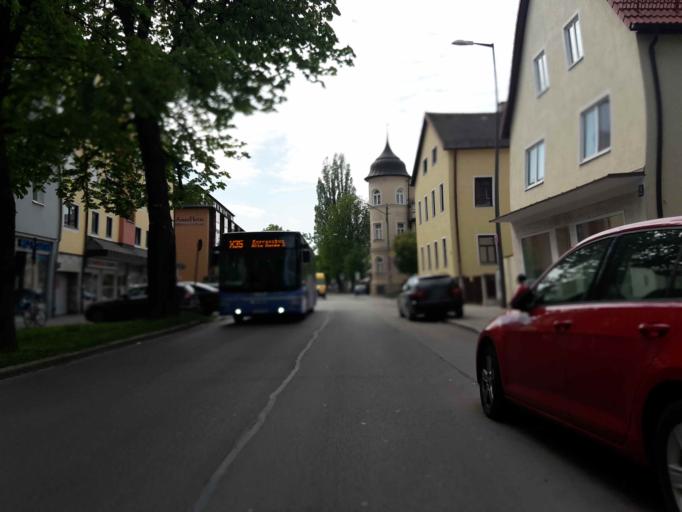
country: DE
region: Bavaria
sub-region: Upper Bavaria
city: Karlsfeld
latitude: 48.1815
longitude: 11.5144
